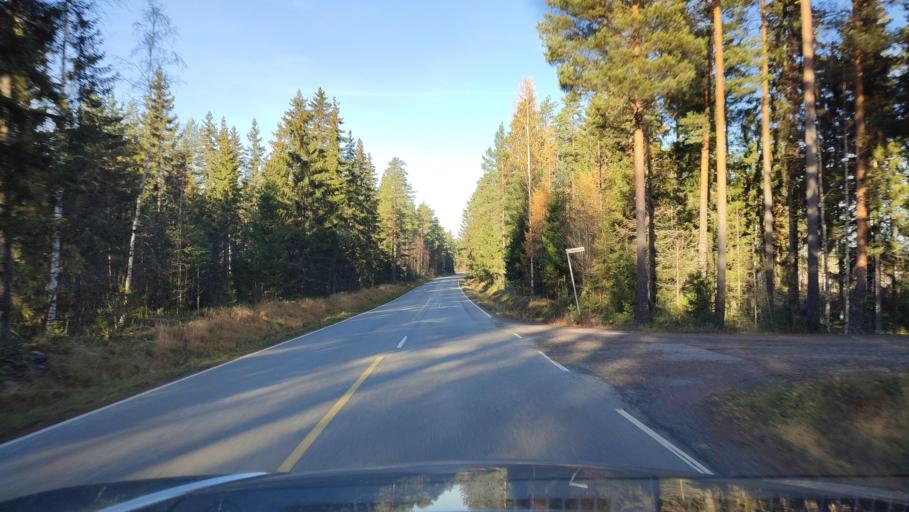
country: FI
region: Southern Ostrobothnia
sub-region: Suupohja
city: Karijoki
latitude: 62.2623
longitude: 21.7332
